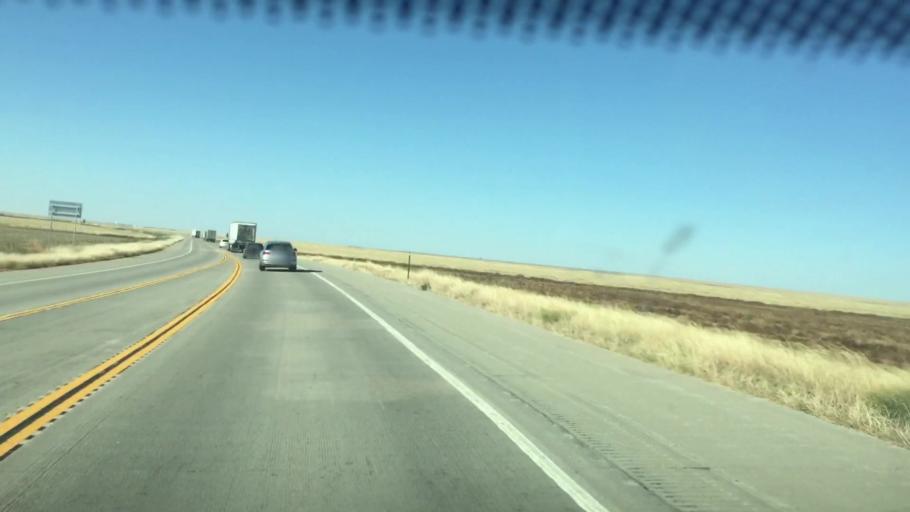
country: US
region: Colorado
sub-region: Kiowa County
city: Eads
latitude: 38.3508
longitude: -102.7143
